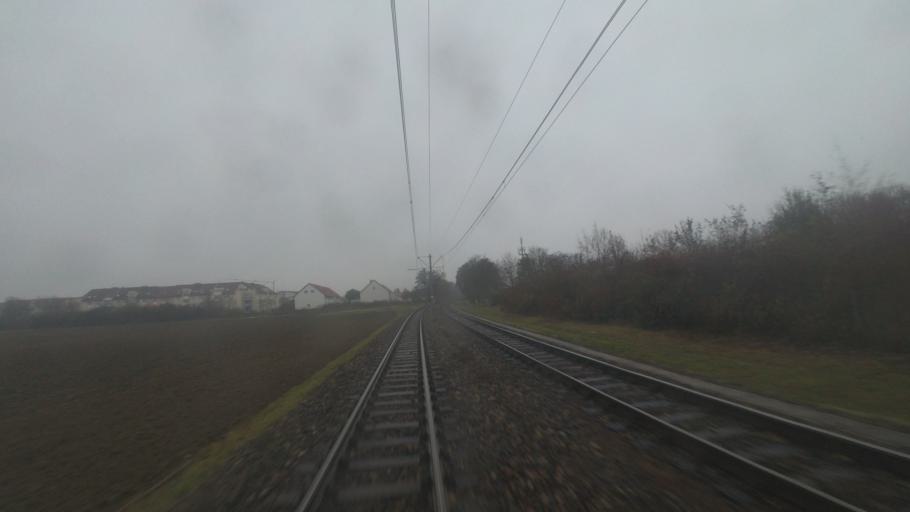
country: DE
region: Rheinland-Pfalz
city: Mutterstadt
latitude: 49.4797
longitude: 8.3370
